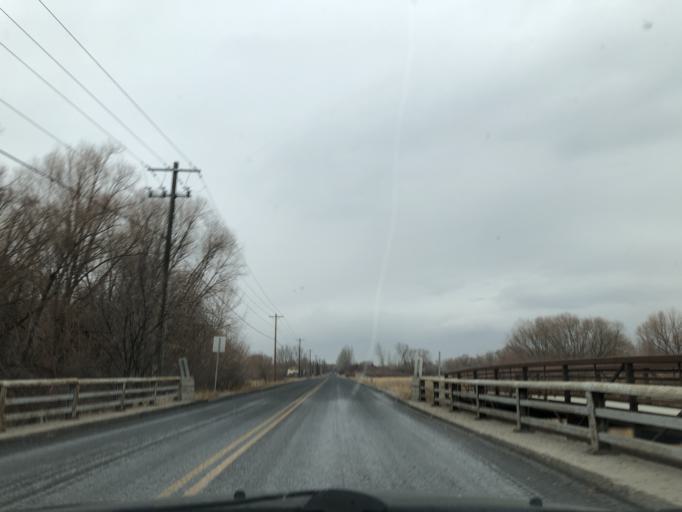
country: US
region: Utah
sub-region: Cache County
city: Logan
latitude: 41.7061
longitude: -111.8531
